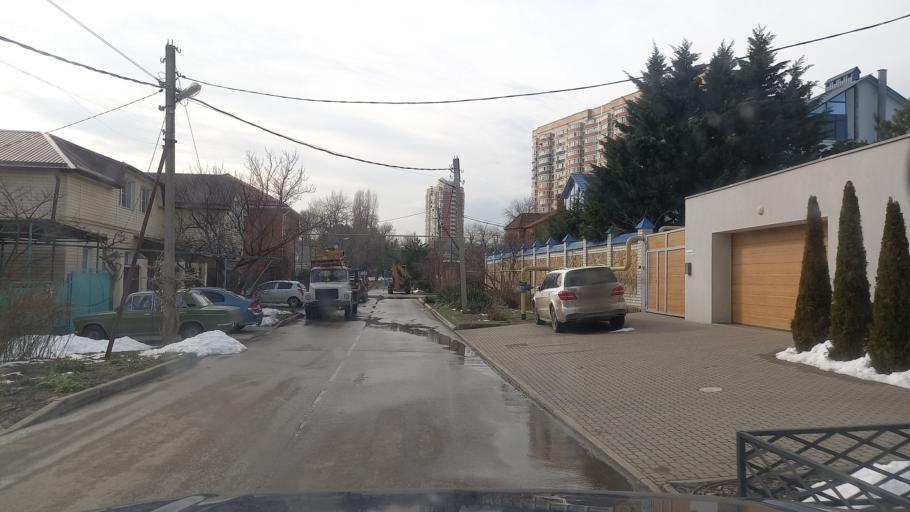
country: RU
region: Adygeya
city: Tlyustenkhabl'
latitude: 45.0102
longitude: 39.0453
